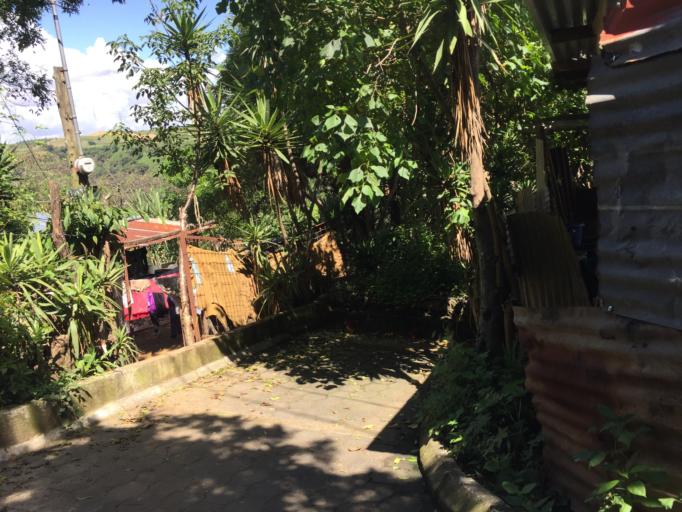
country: GT
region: Guatemala
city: Amatitlan
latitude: 14.4990
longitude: -90.6437
